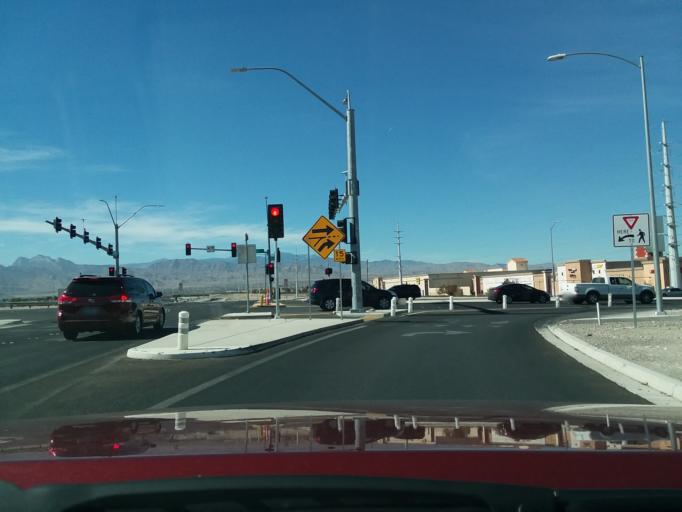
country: US
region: Nevada
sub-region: Clark County
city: North Las Vegas
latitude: 36.2759
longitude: -115.2060
